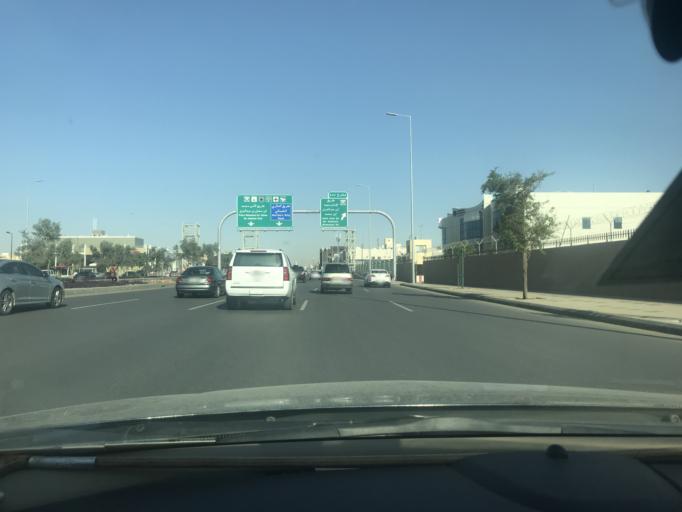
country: SA
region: Ar Riyad
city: Riyadh
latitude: 24.7446
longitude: 46.6814
